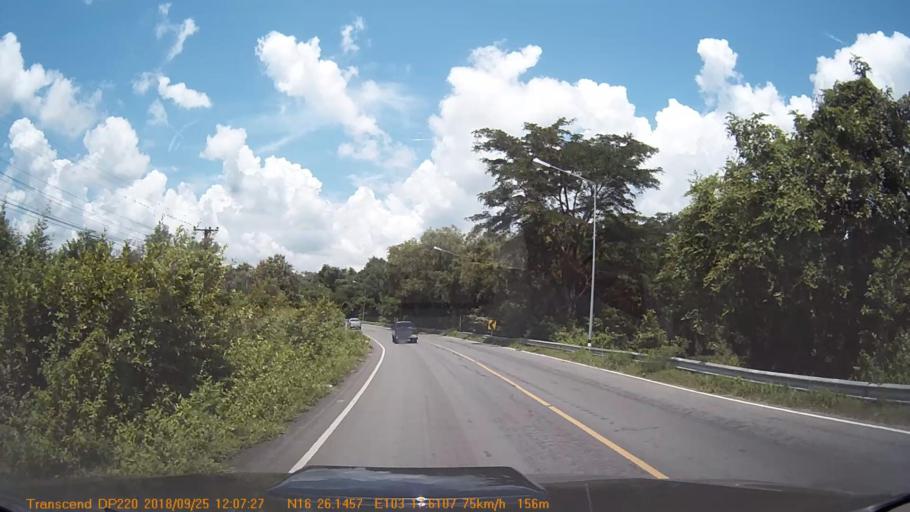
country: TH
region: Kalasin
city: Yang Talat
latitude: 16.4356
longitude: 103.2935
